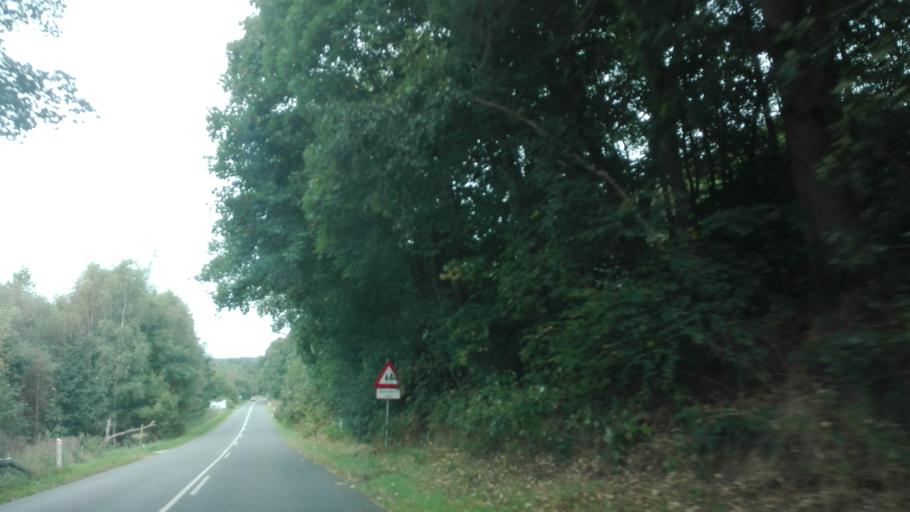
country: DK
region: Central Jutland
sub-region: Skanderborg Kommune
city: Stilling
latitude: 56.0841
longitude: 9.9895
